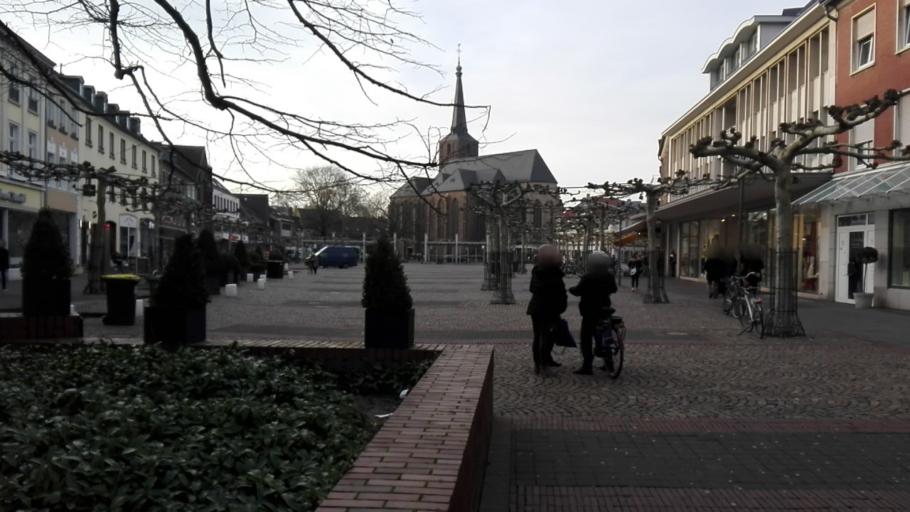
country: DE
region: North Rhine-Westphalia
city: Geldern
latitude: 51.5167
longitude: 6.3234
